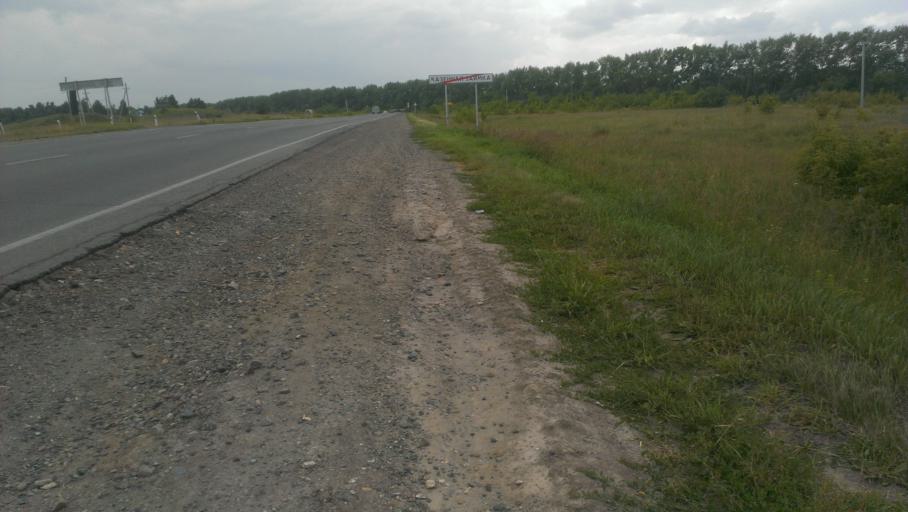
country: RU
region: Altai Krai
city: Gon'ba
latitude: 53.3895
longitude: 83.6014
